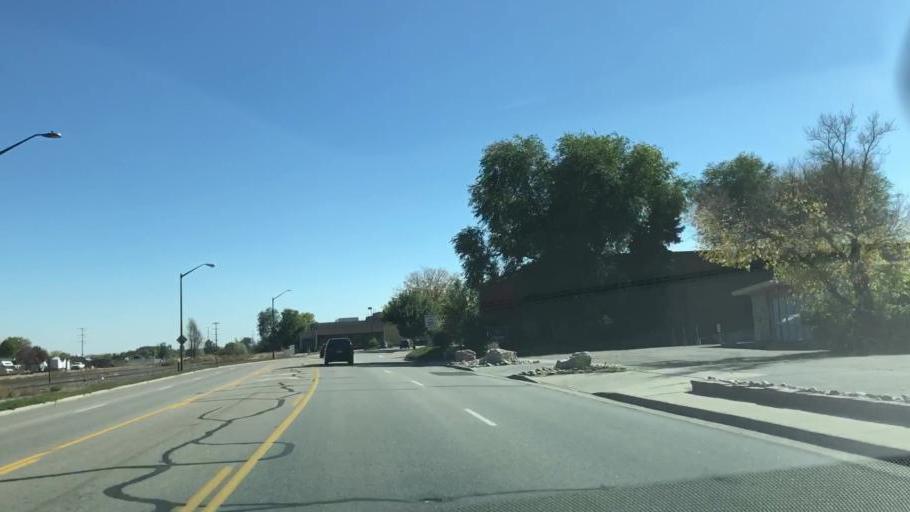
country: US
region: Colorado
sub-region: Larimer County
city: Fort Collins
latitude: 40.5770
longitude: -105.0563
